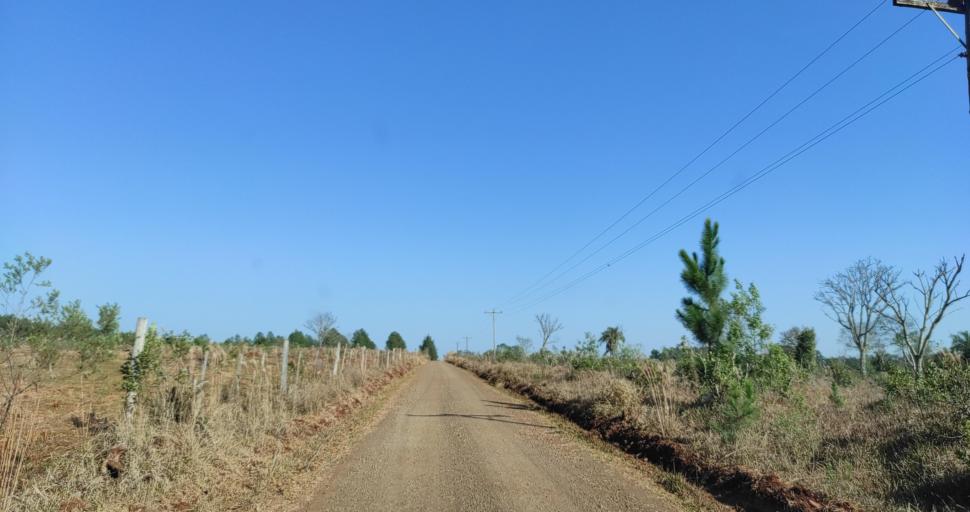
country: AR
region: Misiones
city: Capiovi
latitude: -26.8937
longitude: -55.0436
